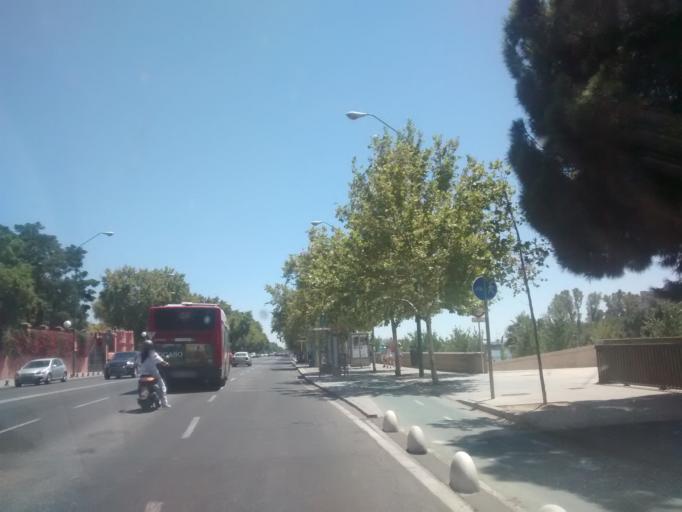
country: ES
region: Andalusia
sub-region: Provincia de Sevilla
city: Sevilla
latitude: 37.3797
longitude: -5.9943
